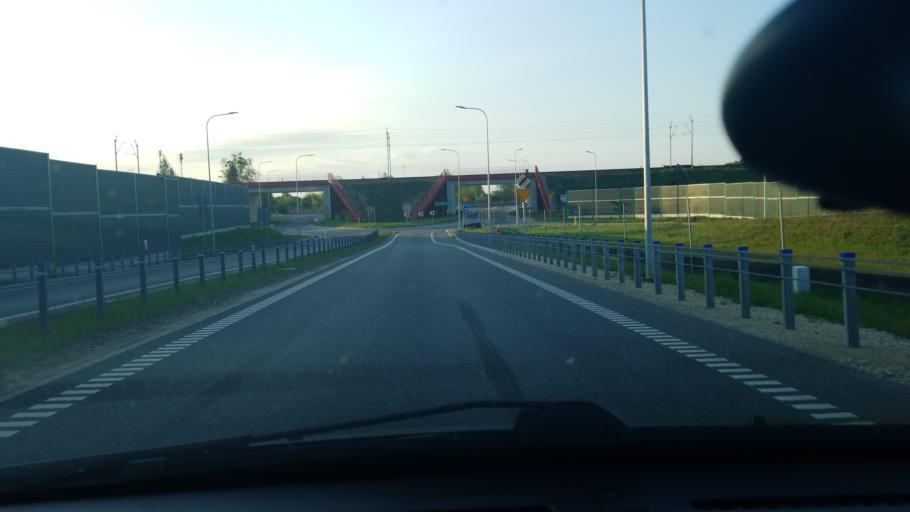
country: PL
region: Silesian Voivodeship
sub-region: Powiat czestochowski
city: Blachownia
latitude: 50.7837
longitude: 19.0100
